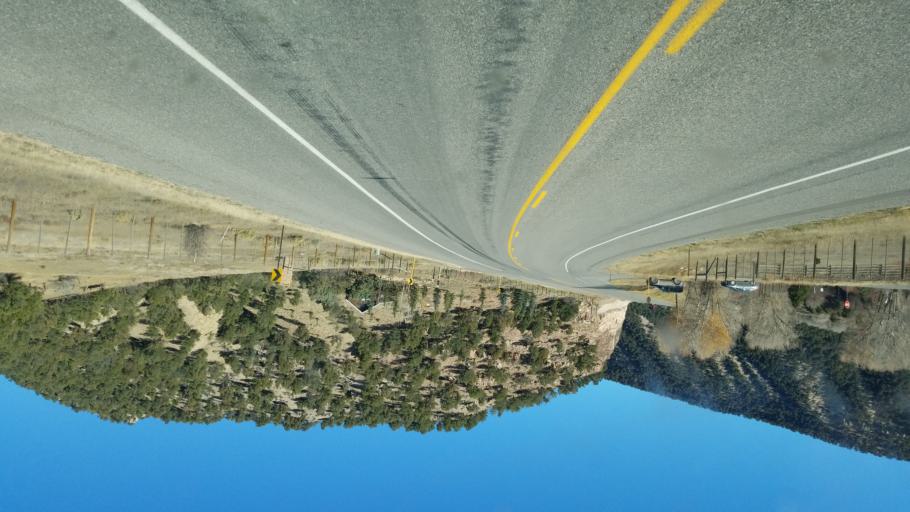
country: US
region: Colorado
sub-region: Ouray County
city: Ouray
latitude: 38.1825
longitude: -107.7440
